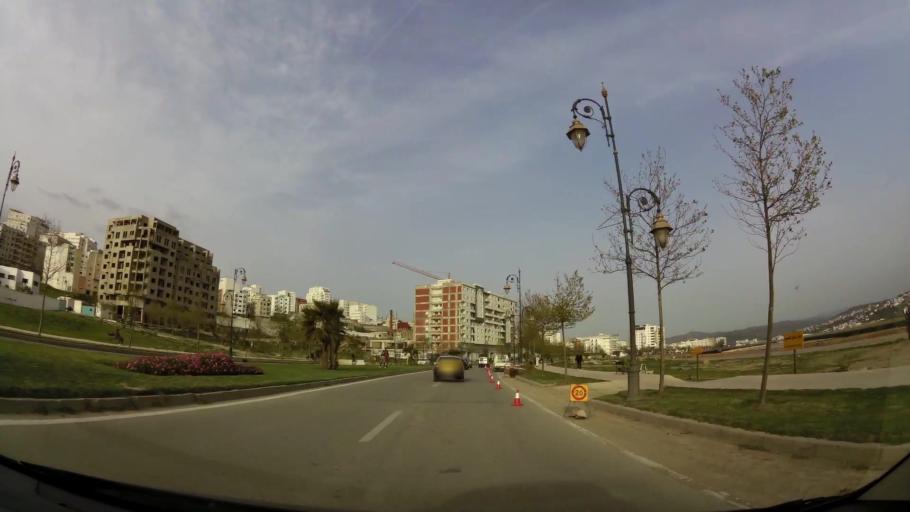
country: MA
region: Tanger-Tetouan
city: Tetouan
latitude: 35.5662
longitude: -5.3872
